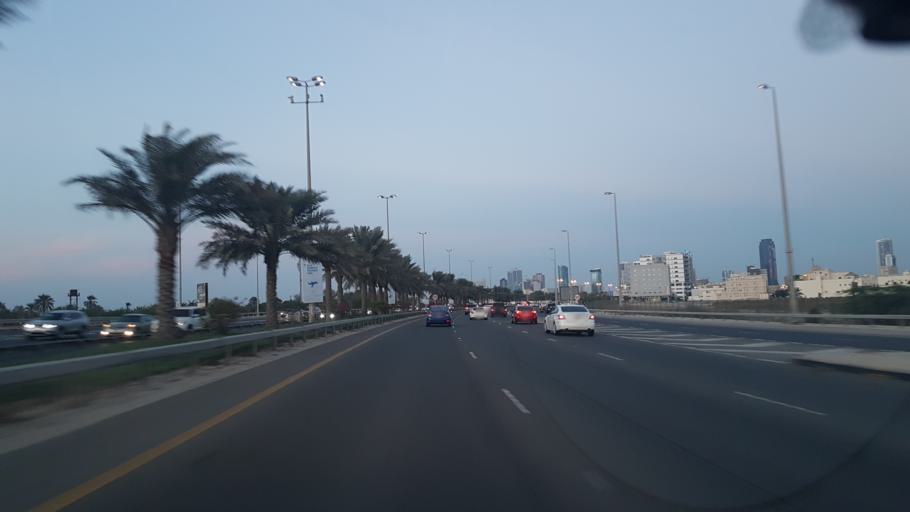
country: BH
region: Manama
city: Jidd Hafs
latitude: 26.2225
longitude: 50.5227
